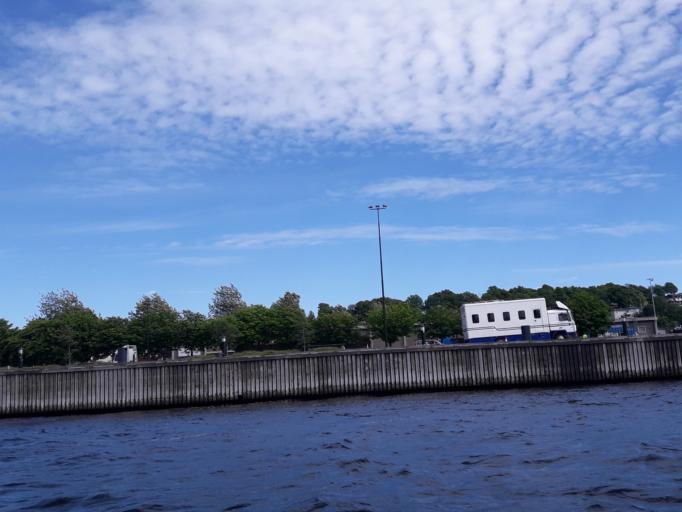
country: NO
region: Ostfold
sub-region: Moss
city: Moss
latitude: 59.4307
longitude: 10.6531
